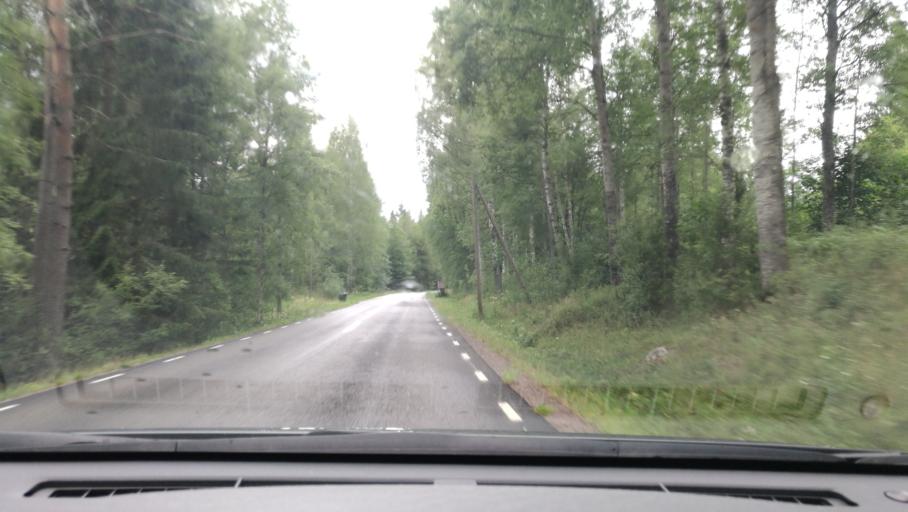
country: SE
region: OEstergoetland
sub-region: Norrkopings Kommun
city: Jursla
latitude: 58.8115
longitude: 16.0912
